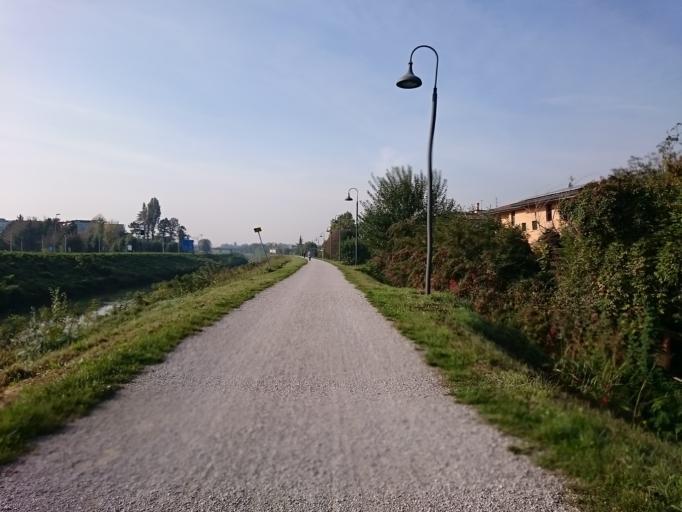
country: IT
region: Veneto
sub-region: Provincia di Padova
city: Mandriola-Sant'Agostino
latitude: 45.3798
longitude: 11.8536
